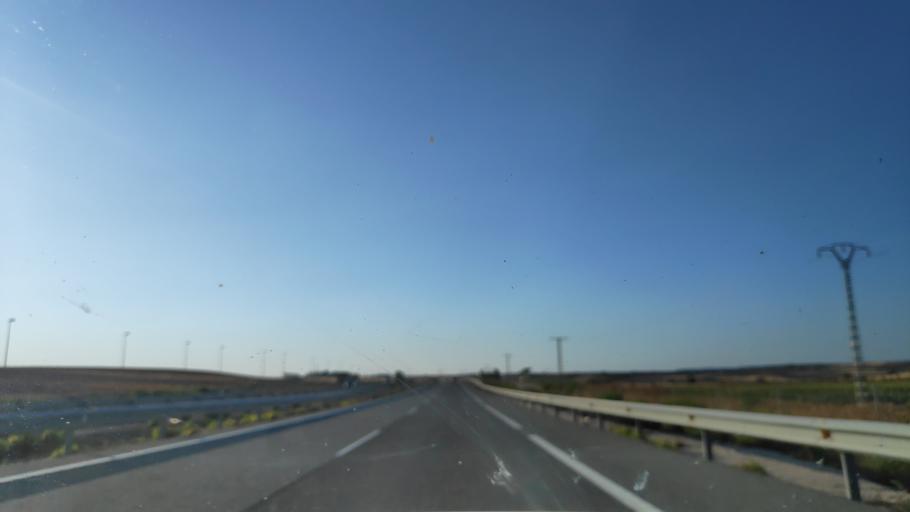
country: ES
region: Castille-La Mancha
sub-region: Provincia de Cuenca
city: Tarancon
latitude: 39.9851
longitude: -2.9640
